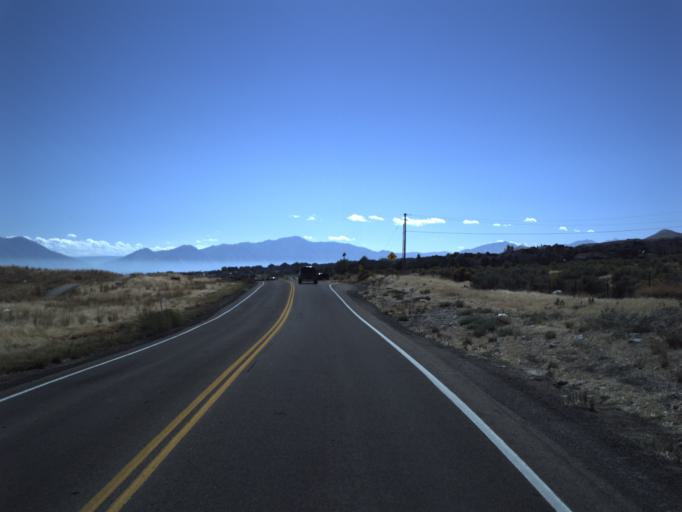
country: US
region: Utah
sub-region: Utah County
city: Saratoga Springs
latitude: 40.3278
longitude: -111.9070
